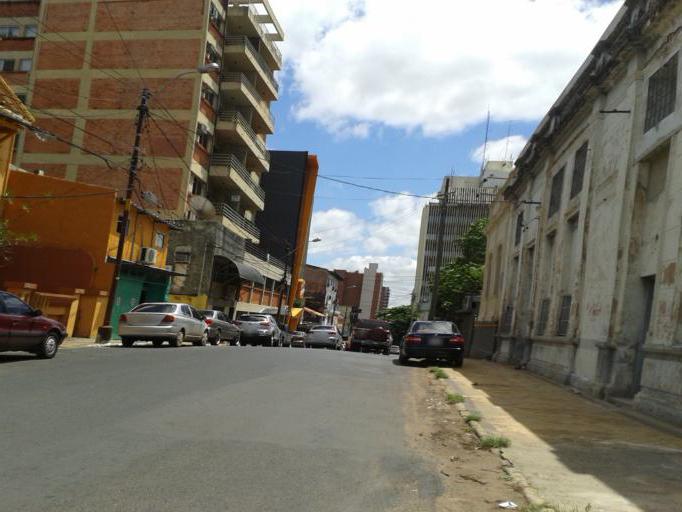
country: PY
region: Asuncion
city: Asuncion
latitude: -25.2892
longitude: -57.6340
